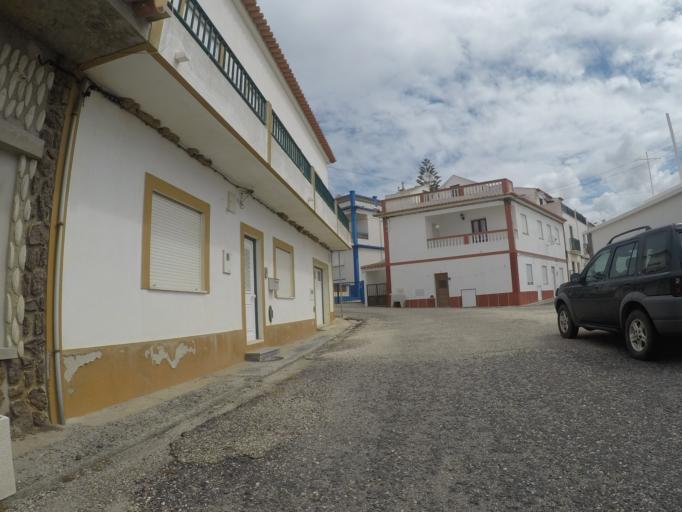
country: PT
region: Beja
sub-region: Odemira
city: Sao Teotonio
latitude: 37.5254
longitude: -8.7869
